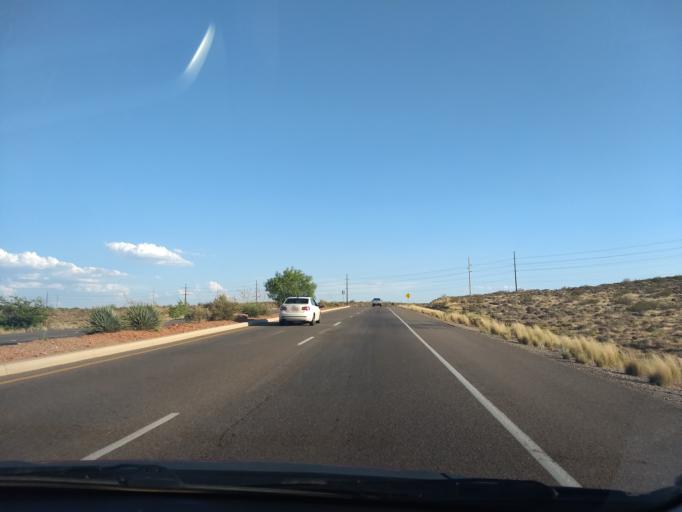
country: US
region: Utah
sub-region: Washington County
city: Saint George
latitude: 37.1281
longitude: -113.5829
